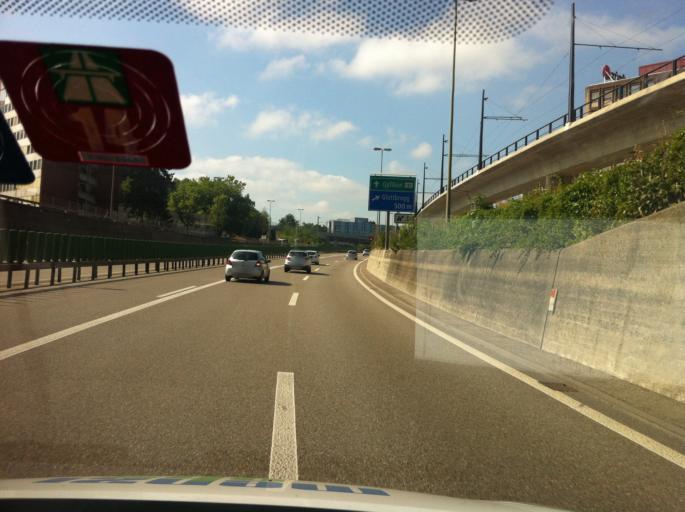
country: CH
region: Zurich
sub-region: Bezirk Buelach
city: Kloten / Balsberg
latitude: 47.4456
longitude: 8.5709
